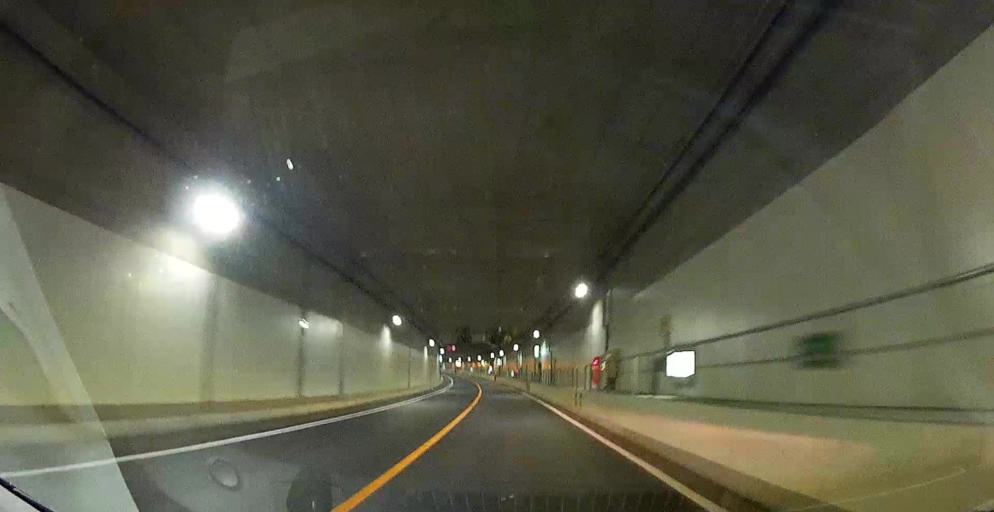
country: JP
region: Tokyo
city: Urayasu
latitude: 35.6157
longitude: 139.7961
